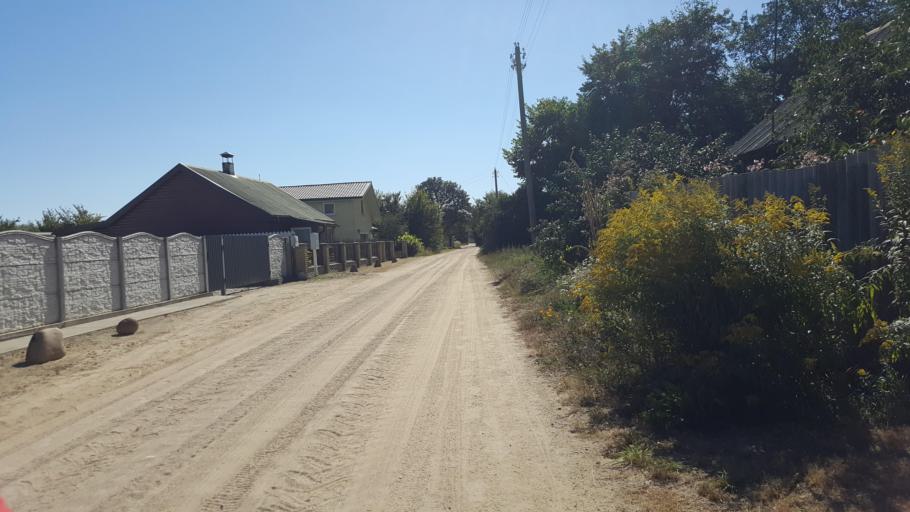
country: PL
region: Lublin Voivodeship
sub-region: Powiat bialski
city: Rokitno
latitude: 52.2220
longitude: 23.3429
